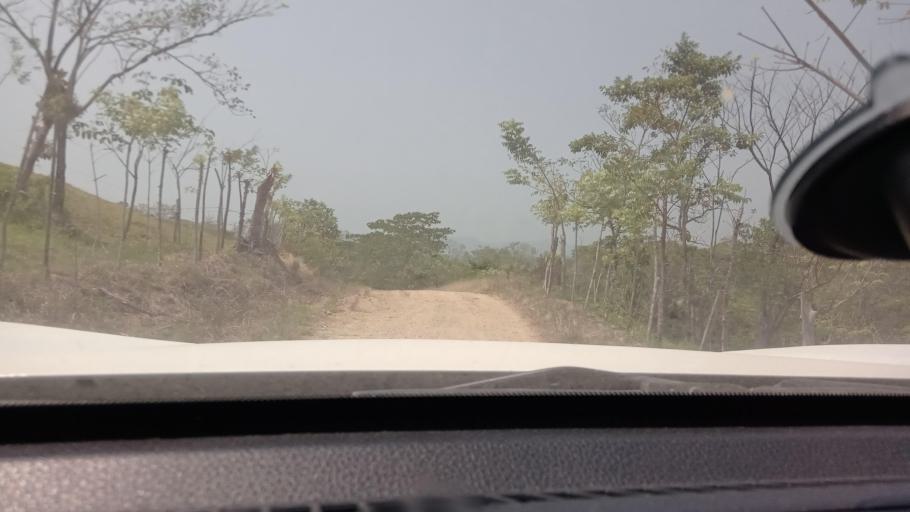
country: MX
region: Tabasco
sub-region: Huimanguillo
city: Francisco Rueda
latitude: 17.4916
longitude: -93.9305
